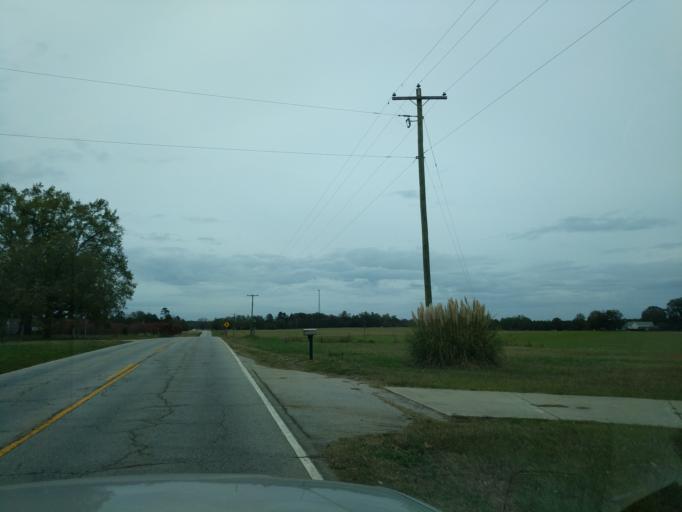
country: US
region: South Carolina
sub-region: Saluda County
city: Saluda
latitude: 34.0990
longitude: -81.7520
